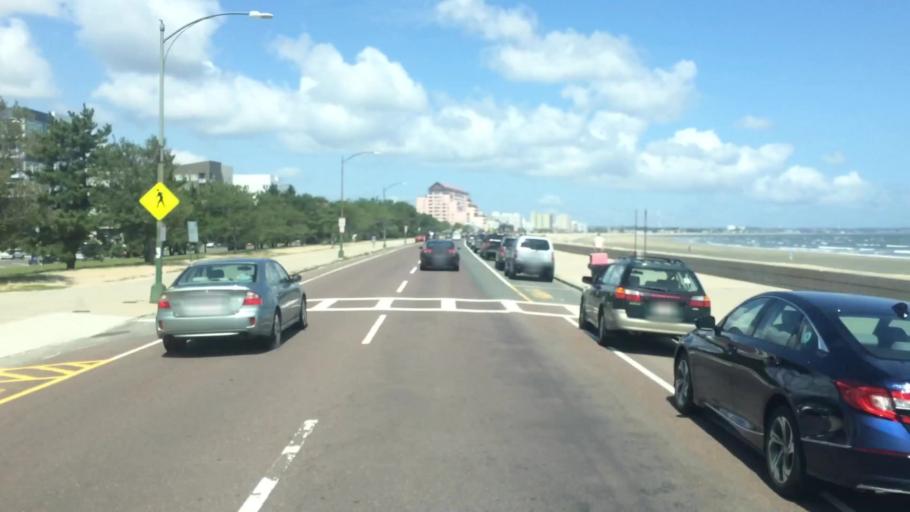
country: US
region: Massachusetts
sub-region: Suffolk County
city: Revere
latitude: 42.4145
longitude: -70.9892
